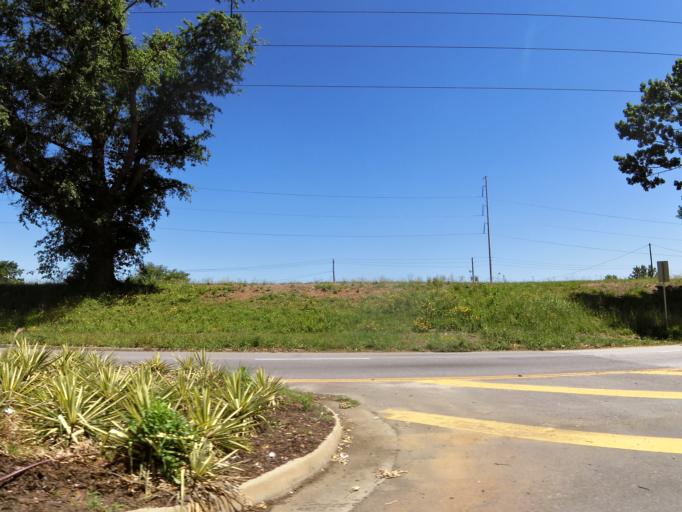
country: US
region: Georgia
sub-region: Richmond County
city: Augusta
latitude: 33.4724
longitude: -81.9798
